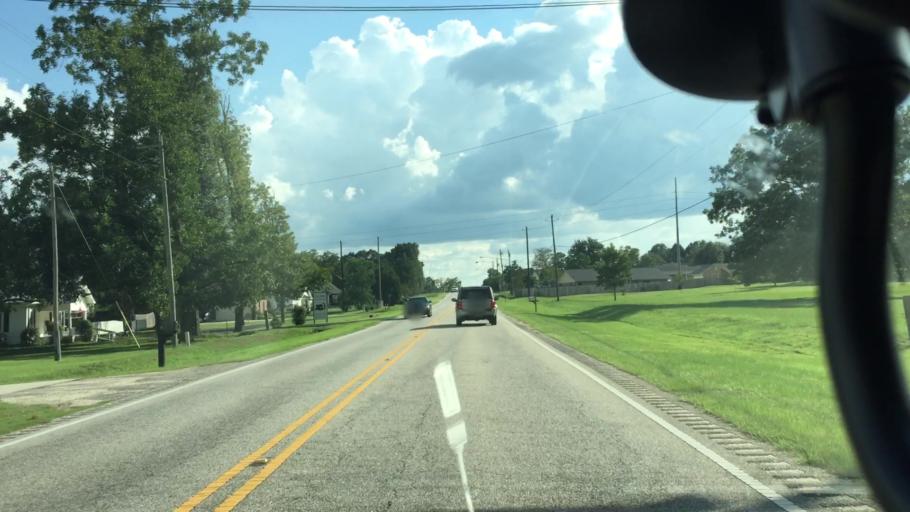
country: US
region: Alabama
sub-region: Coffee County
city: Enterprise
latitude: 31.3676
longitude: -85.8275
